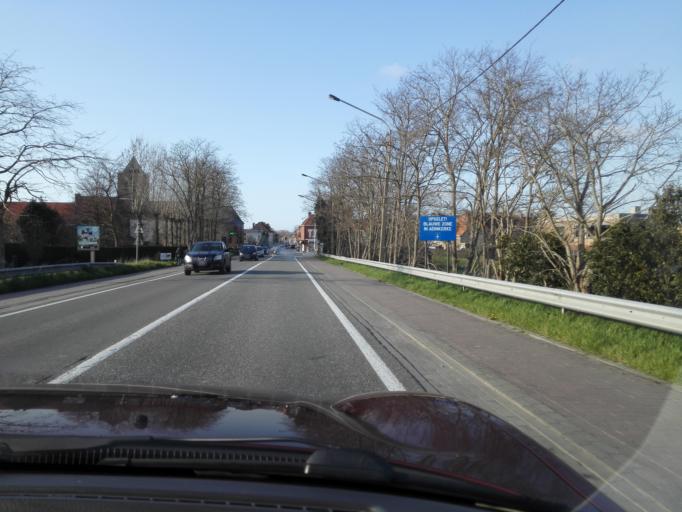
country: BE
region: Flanders
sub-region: Provincie West-Vlaanderen
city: De Panne
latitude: 51.0739
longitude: 2.6036
